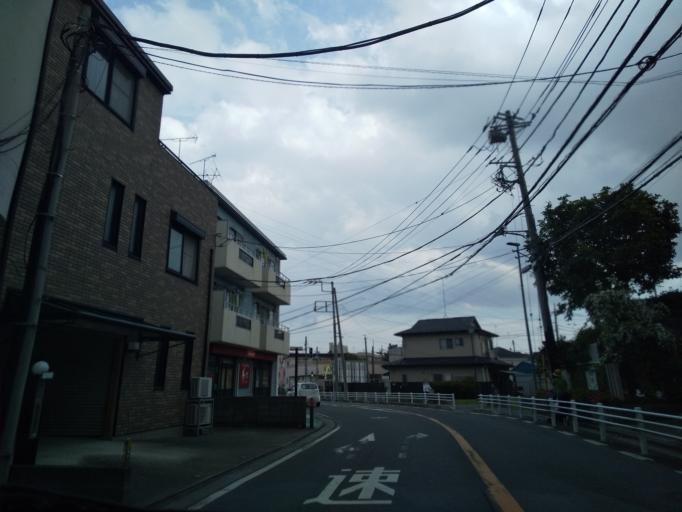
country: JP
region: Kanagawa
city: Zama
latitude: 35.5256
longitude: 139.4067
